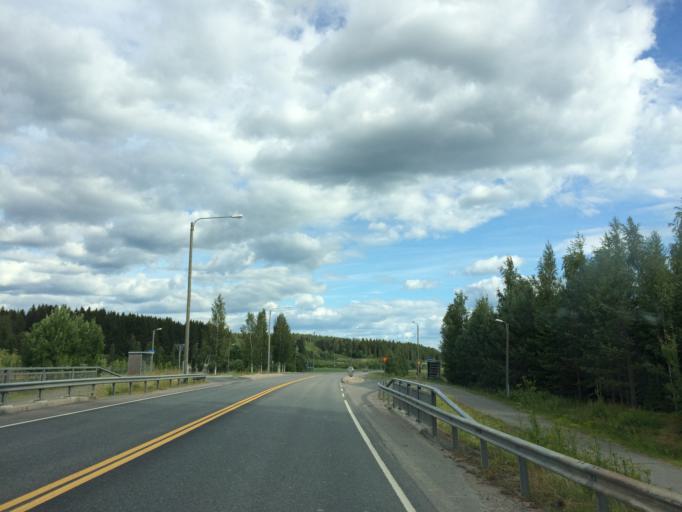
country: FI
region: Haeme
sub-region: Haemeenlinna
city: Turenki
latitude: 60.9550
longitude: 24.6010
